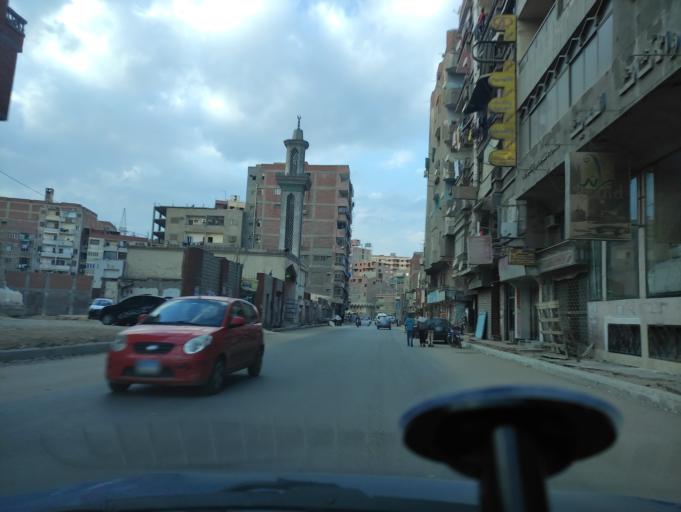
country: EG
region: Muhafazat al Qalyubiyah
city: Al Khankah
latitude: 30.1309
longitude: 31.3610
